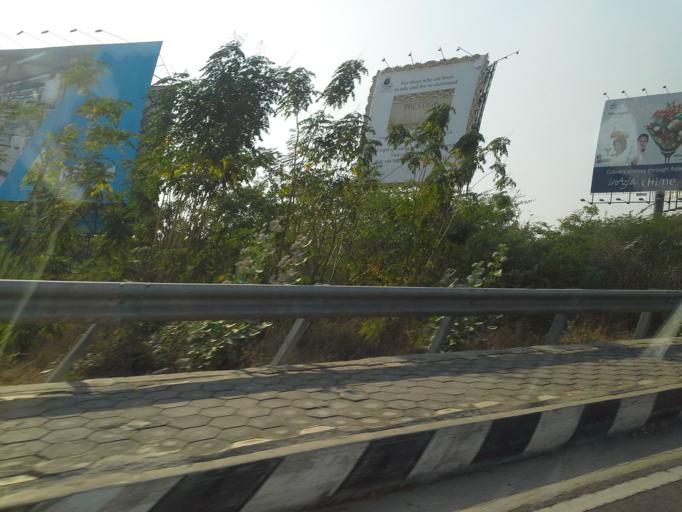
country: IN
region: Telangana
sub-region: Rangareddi
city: Sriramnagar
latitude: 17.2455
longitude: 78.3834
